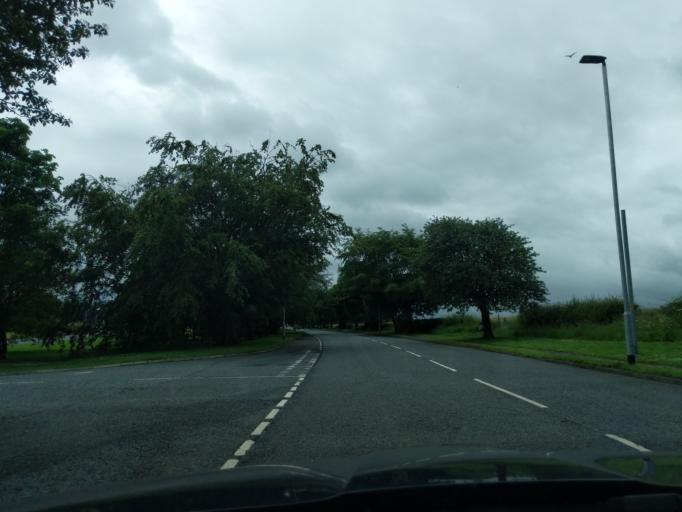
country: GB
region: England
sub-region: Northumberland
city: Berwick-Upon-Tweed
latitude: 55.7620
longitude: -2.0252
